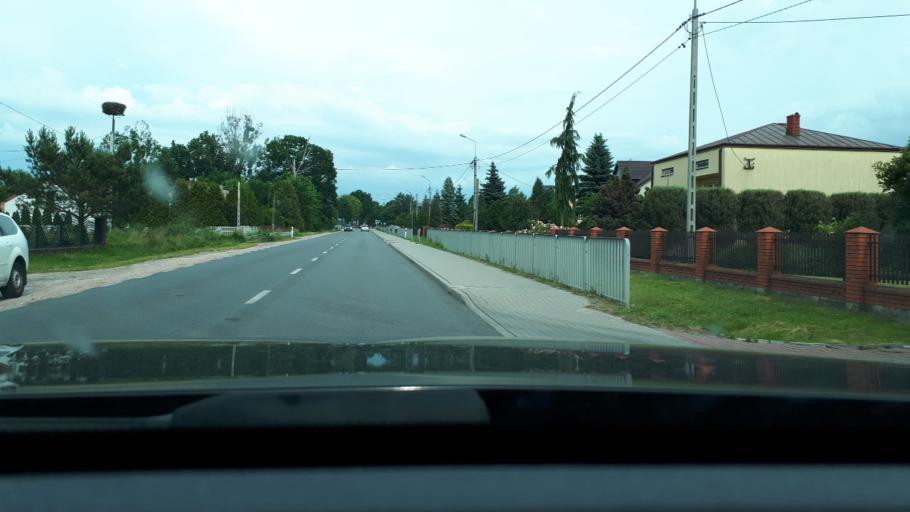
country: PL
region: Masovian Voivodeship
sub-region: Powiat warszawski zachodni
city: Kampinos
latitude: 52.2695
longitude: 20.4373
